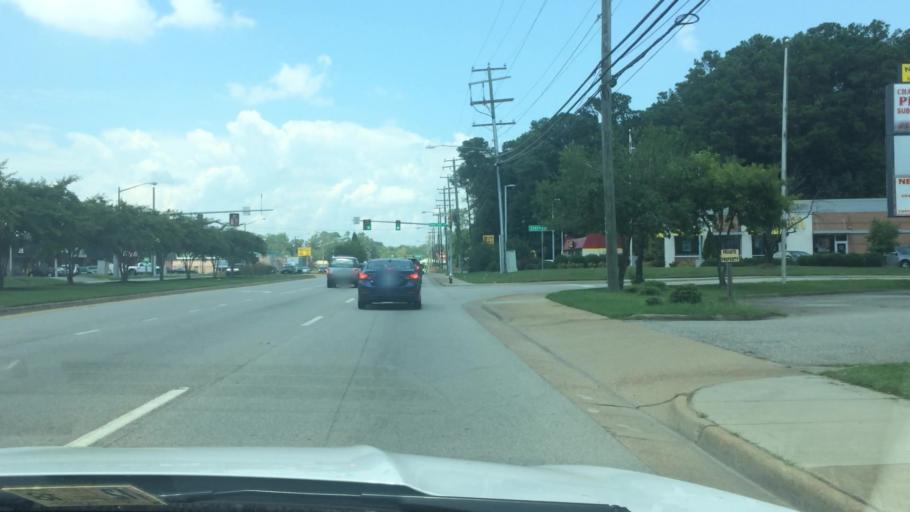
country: US
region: Virginia
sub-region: York County
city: Yorktown
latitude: 37.1555
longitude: -76.5556
